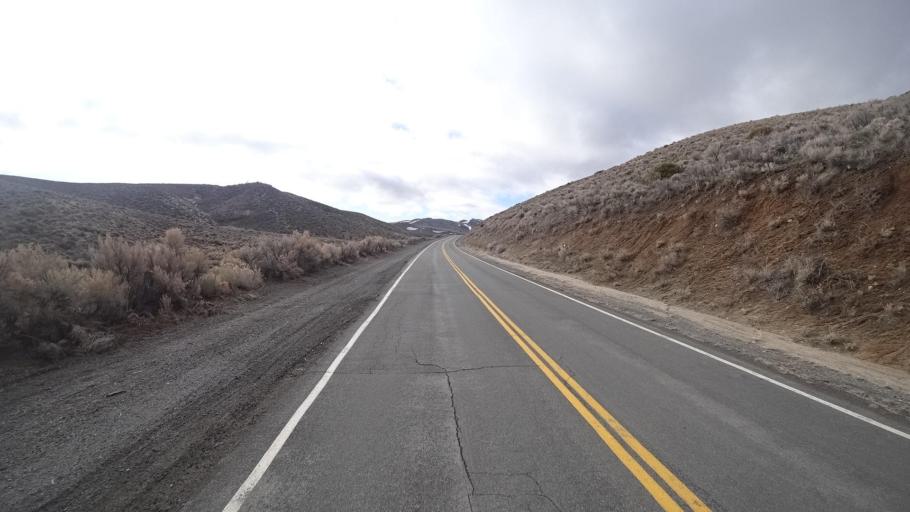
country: US
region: Nevada
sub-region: Washoe County
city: Cold Springs
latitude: 39.8158
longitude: -119.9347
